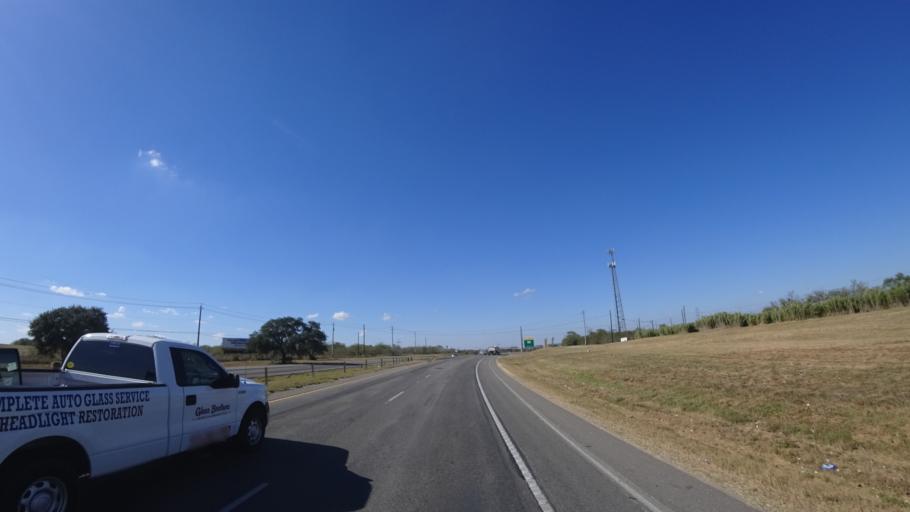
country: US
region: Texas
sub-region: Travis County
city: Garfield
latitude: 30.1863
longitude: -97.6138
